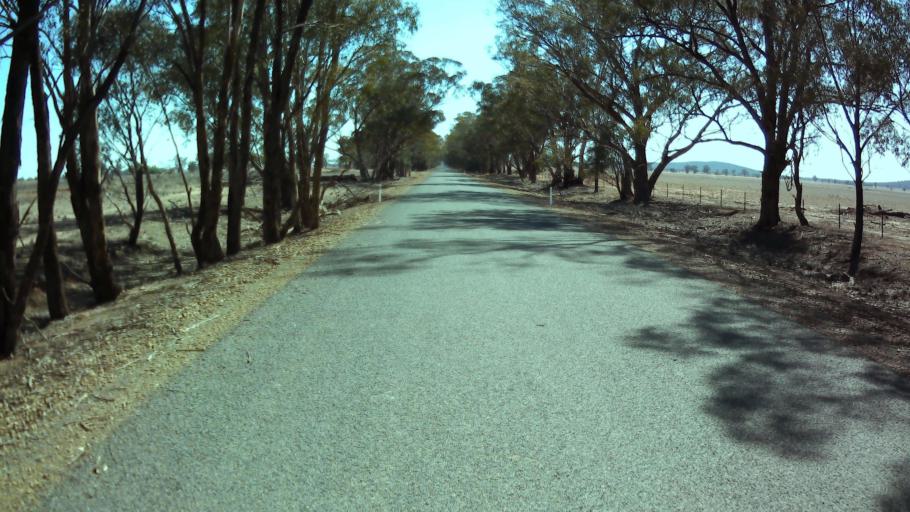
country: AU
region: New South Wales
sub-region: Weddin
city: Grenfell
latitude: -33.7273
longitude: 147.8921
